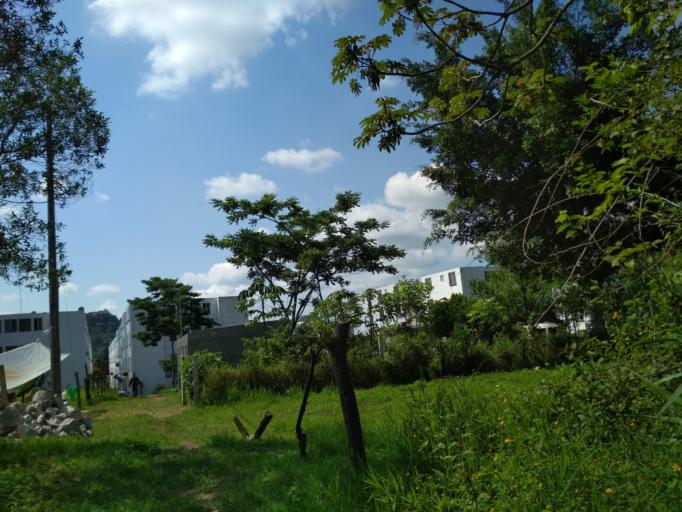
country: MX
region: Veracruz
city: Cordoba
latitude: 18.8743
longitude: -96.9082
